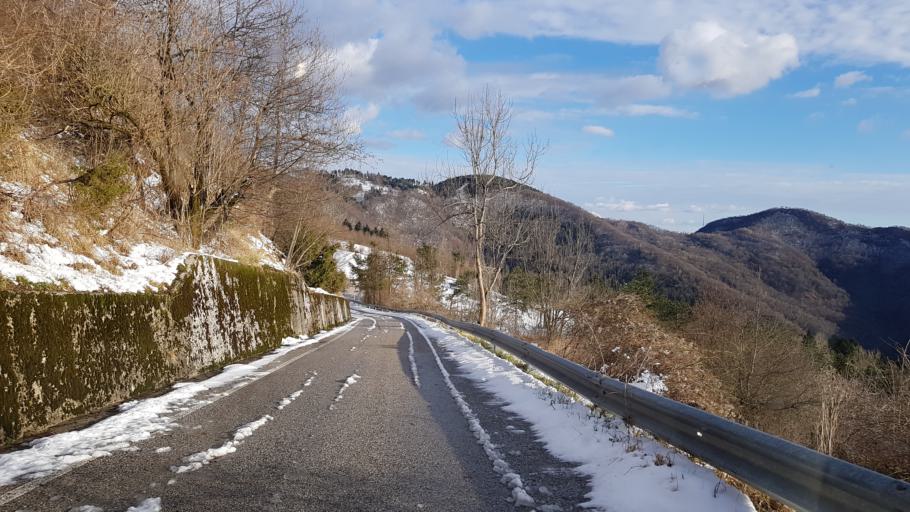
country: IT
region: Friuli Venezia Giulia
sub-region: Provincia di Udine
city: Faedis
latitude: 46.1822
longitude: 13.3918
